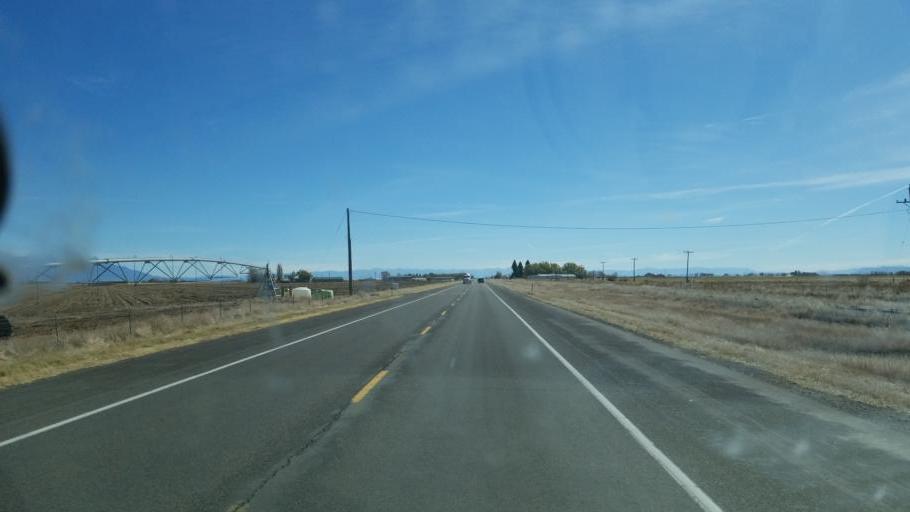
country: US
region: Colorado
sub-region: Rio Grande County
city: Monte Vista
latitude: 37.5552
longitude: -106.0836
